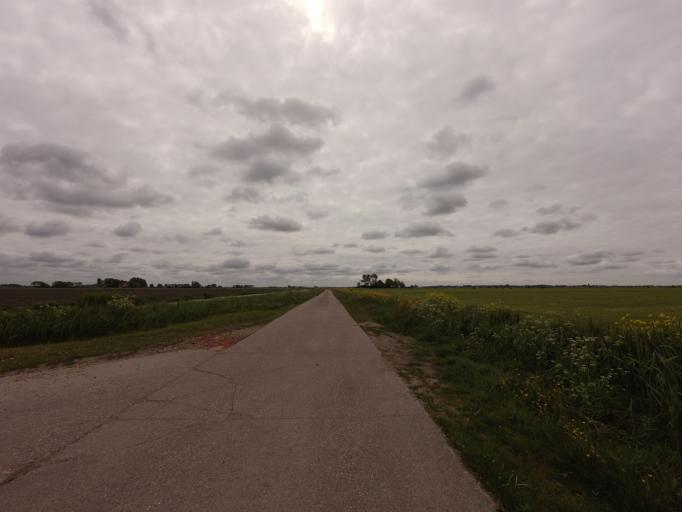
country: NL
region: Friesland
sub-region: Sudwest Fryslan
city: Workum
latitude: 52.9505
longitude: 5.4534
